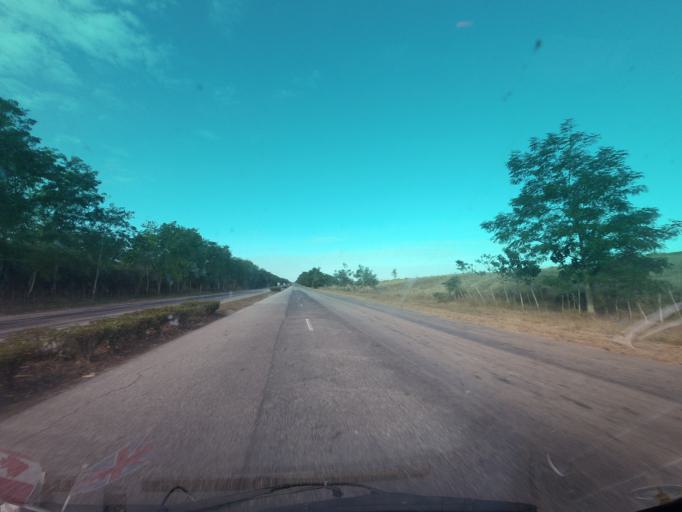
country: CU
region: Cienfuegos
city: Rodas
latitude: 22.4438
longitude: -80.4553
